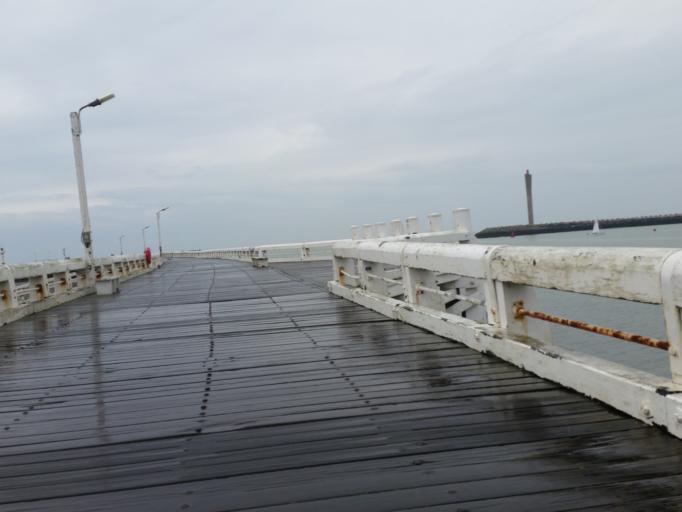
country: BE
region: Flanders
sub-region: Provincie West-Vlaanderen
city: Ostend
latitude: 51.2362
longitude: 2.9221
